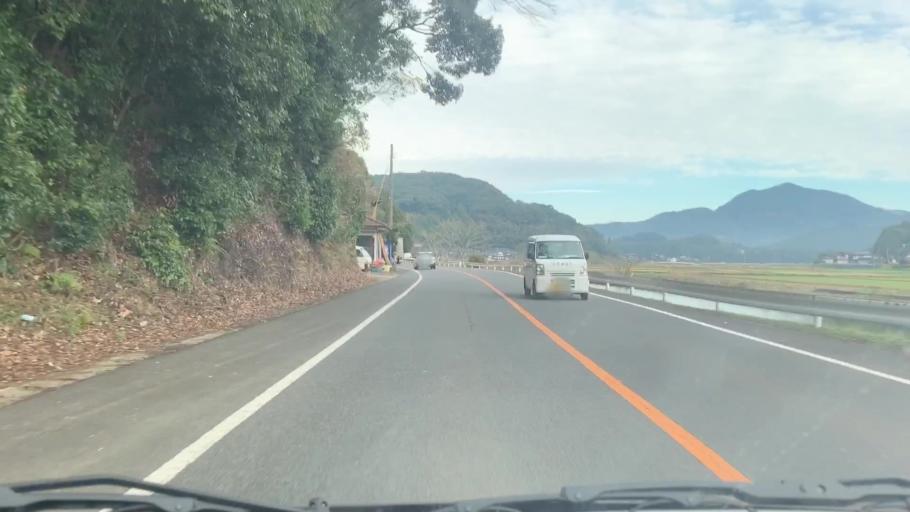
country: JP
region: Saga Prefecture
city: Takeocho-takeo
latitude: 33.2344
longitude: 129.9669
